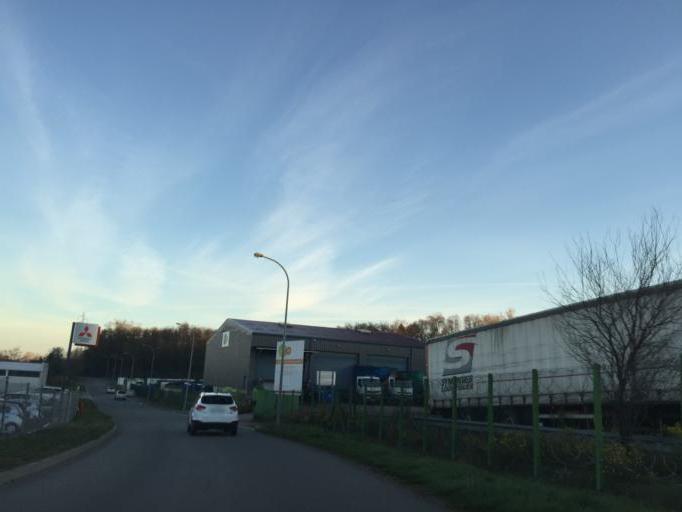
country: FR
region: Rhone-Alpes
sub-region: Departement de la Loire
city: Le Coteau
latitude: 46.0185
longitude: 4.1012
